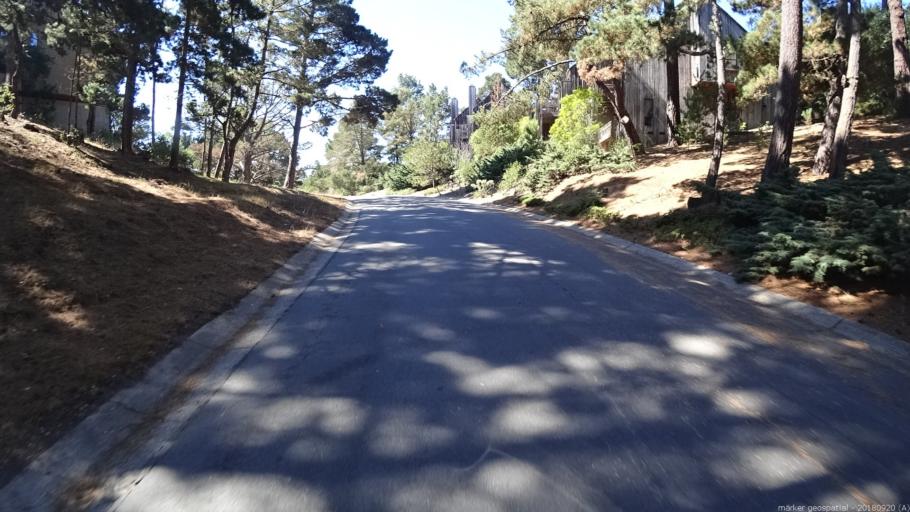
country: US
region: California
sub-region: Monterey County
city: Carmel-by-the-Sea
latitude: 36.5661
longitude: -121.9059
